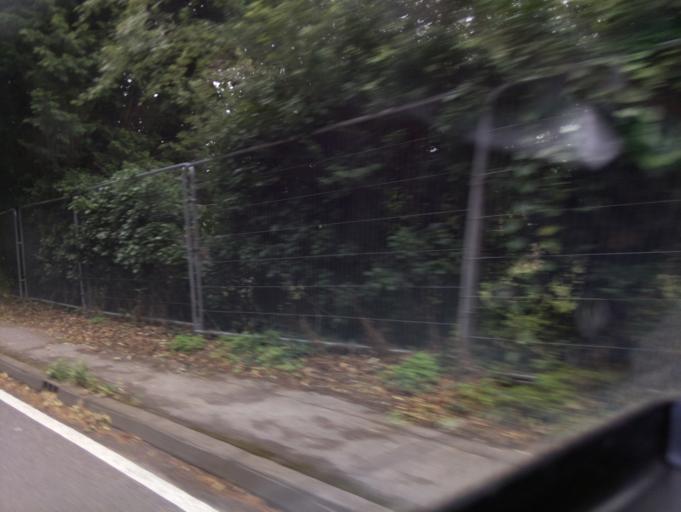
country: GB
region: England
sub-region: Worcestershire
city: Upton upon Severn
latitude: 52.0935
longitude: -2.2081
